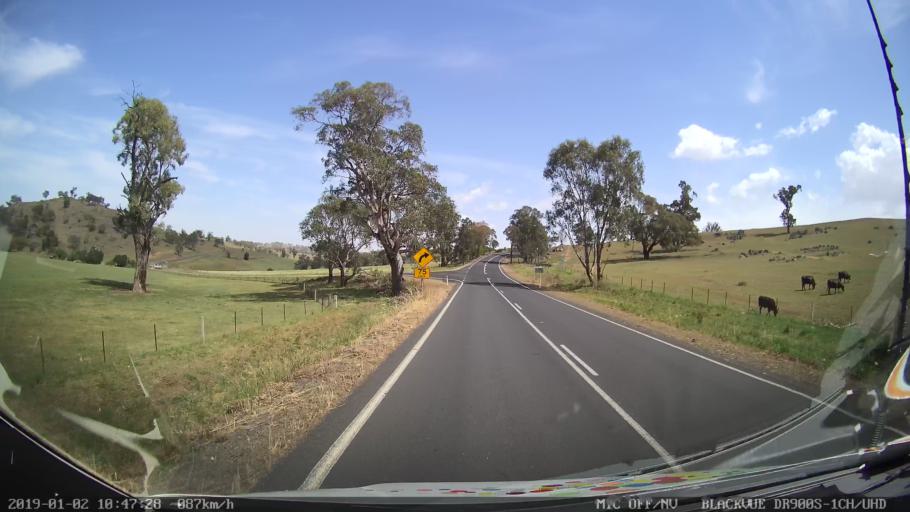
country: AU
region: New South Wales
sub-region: Cootamundra
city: Cootamundra
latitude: -34.7447
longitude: 148.2732
